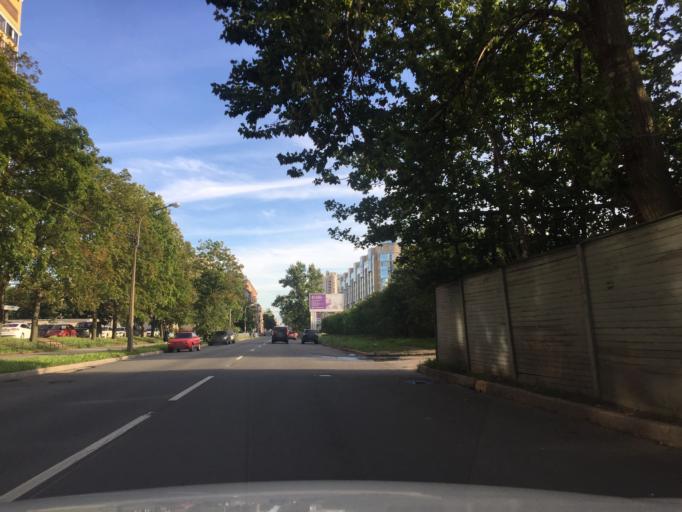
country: RU
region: St.-Petersburg
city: Admiralteisky
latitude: 59.8797
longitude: 30.3132
